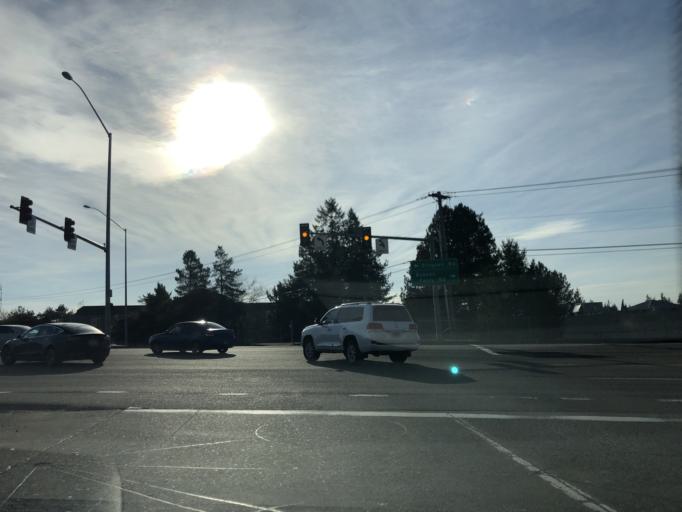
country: US
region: Oregon
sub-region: Clackamas County
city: Wilsonville
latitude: 45.3370
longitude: -122.7714
